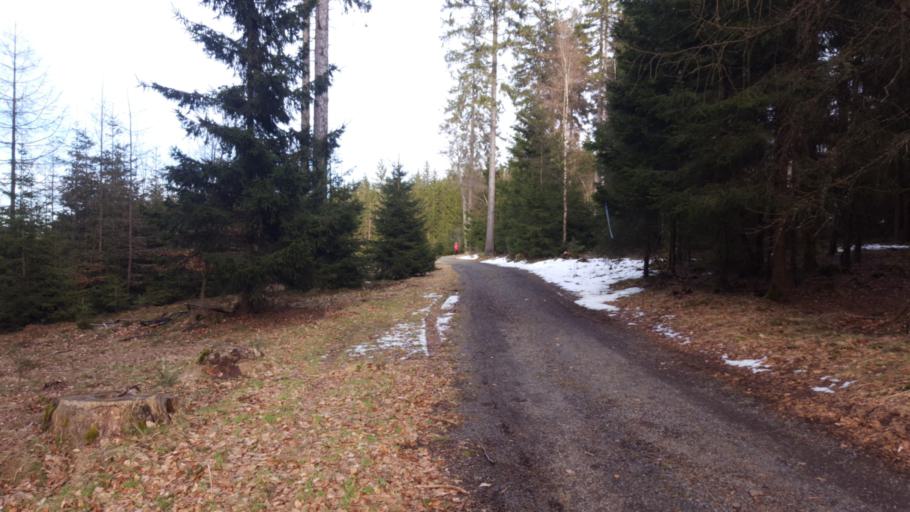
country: CZ
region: Karlovarsky
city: As
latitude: 50.2369
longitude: 12.1994
